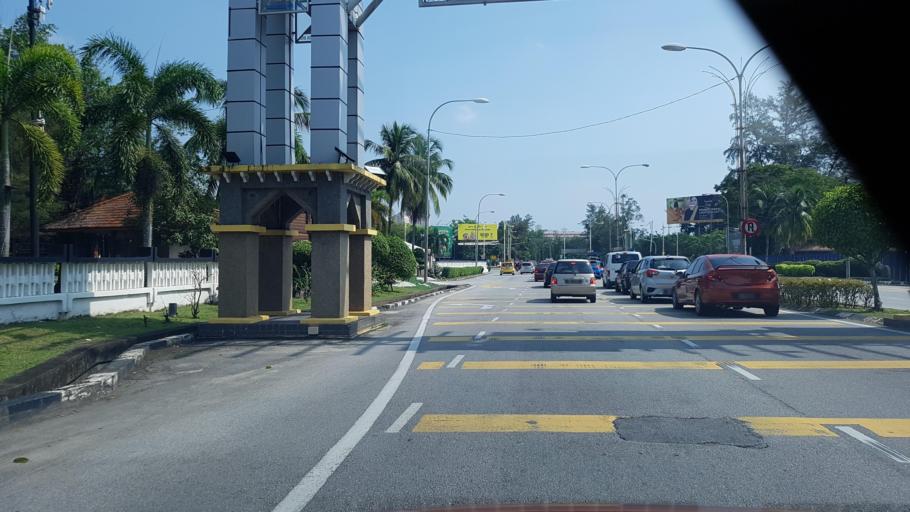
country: MY
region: Terengganu
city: Kuala Terengganu
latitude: 5.3177
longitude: 103.1537
